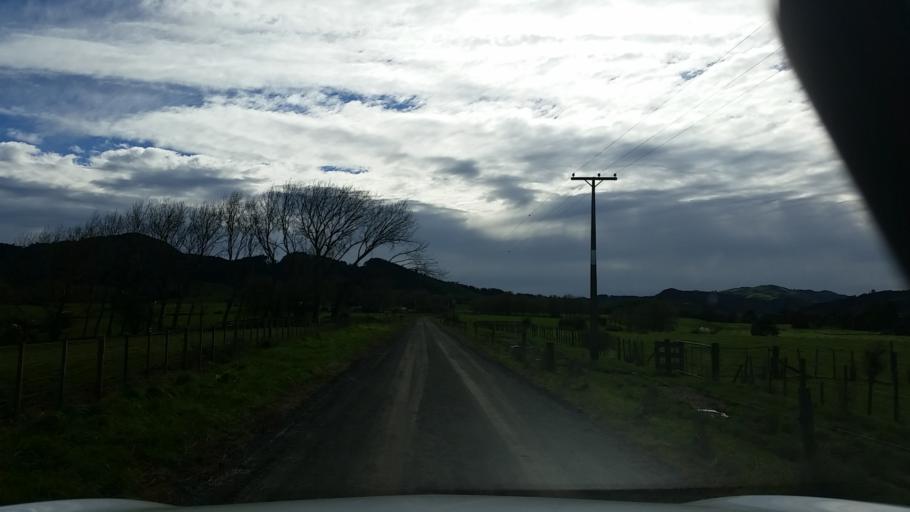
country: NZ
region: Waikato
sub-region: Hauraki District
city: Ngatea
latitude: -37.5080
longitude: 175.4074
